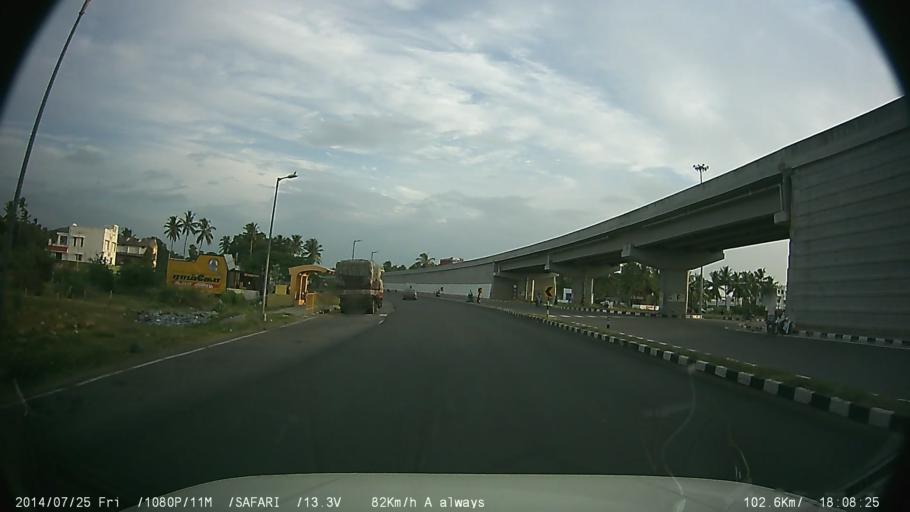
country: IN
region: Tamil Nadu
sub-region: Krishnagiri
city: Kaverippattanam
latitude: 12.4015
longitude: 78.2186
